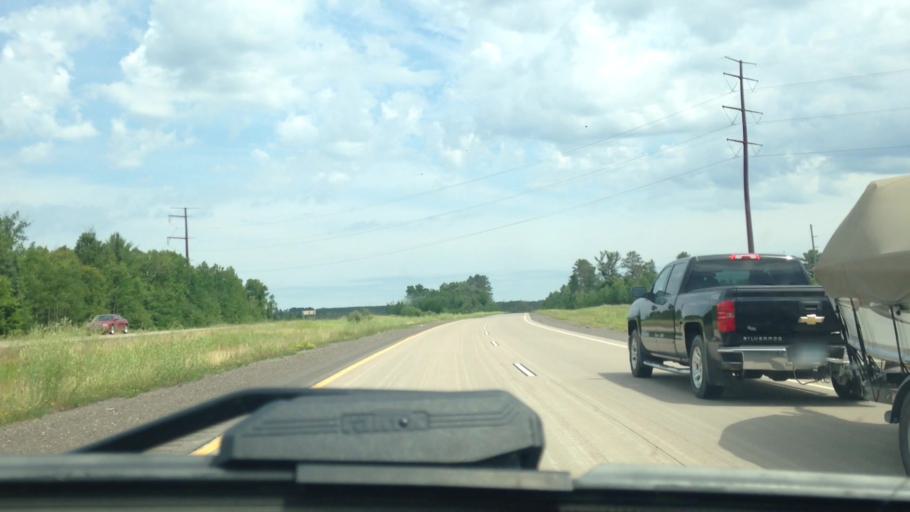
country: US
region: Wisconsin
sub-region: Douglas County
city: Lake Nebagamon
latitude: 46.2550
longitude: -91.8019
